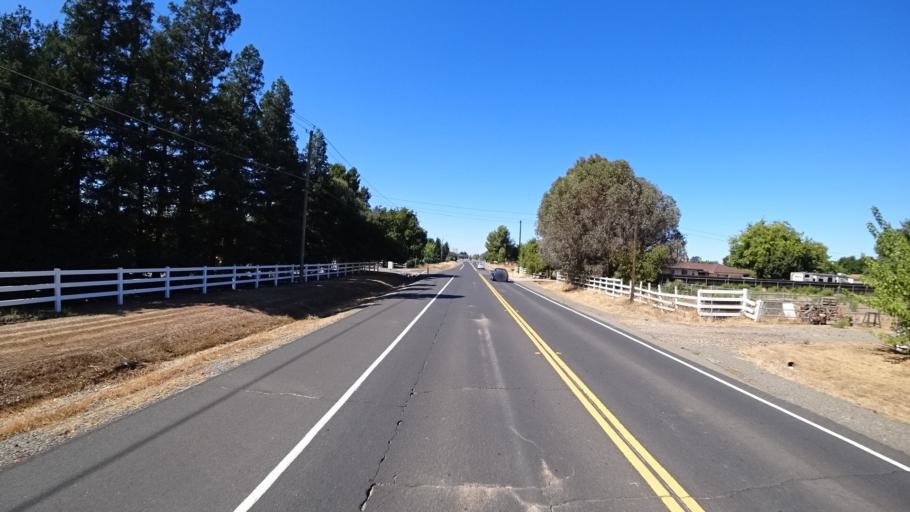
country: US
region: California
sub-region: Sacramento County
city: Elk Grove
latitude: 38.4381
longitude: -121.3660
